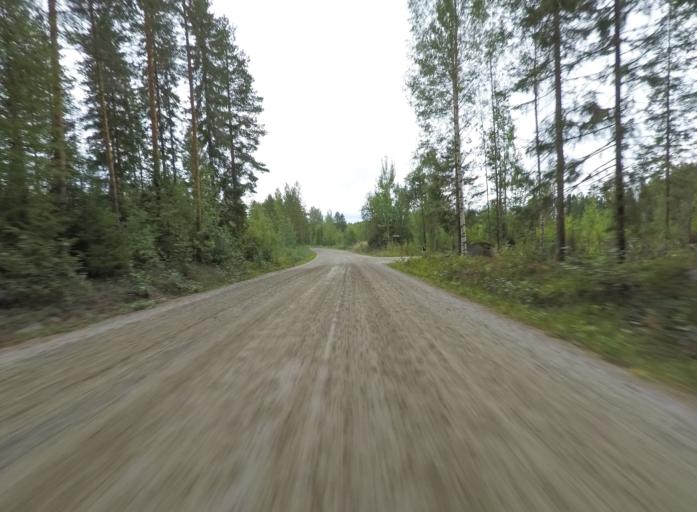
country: FI
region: Central Finland
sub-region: Jyvaeskylae
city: Hankasalmi
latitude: 62.4033
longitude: 26.6026
